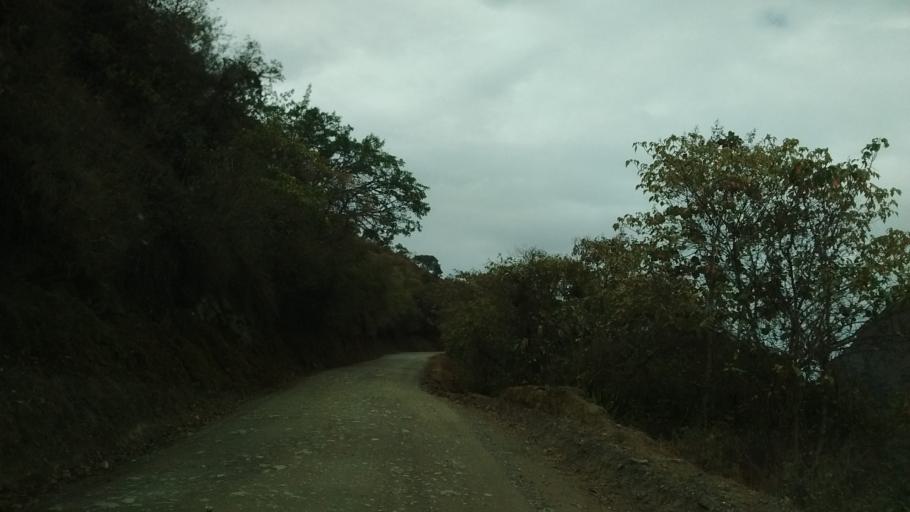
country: CO
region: Cauca
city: Almaguer
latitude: 1.8583
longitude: -76.9366
